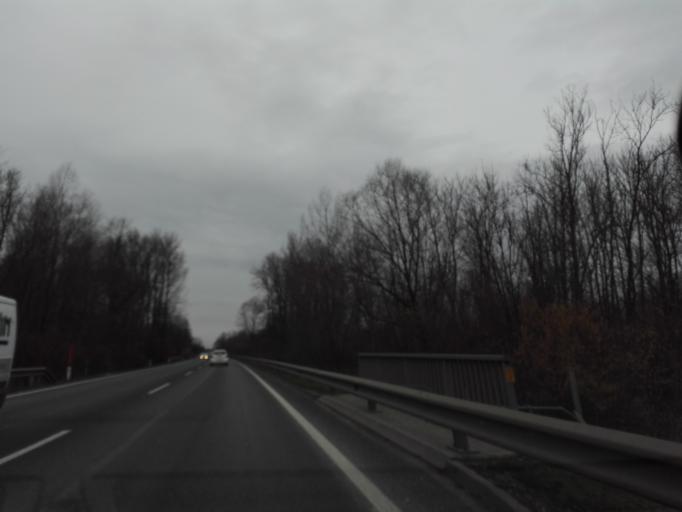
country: AT
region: Upper Austria
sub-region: Politischer Bezirk Linz-Land
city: Traun
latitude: 48.2129
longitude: 14.2378
